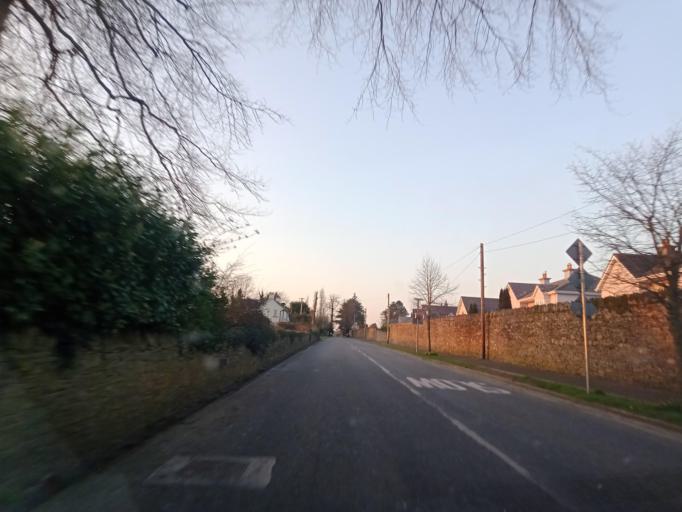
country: IE
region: Leinster
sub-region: Laois
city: Abbeyleix
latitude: 52.8770
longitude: -7.3088
